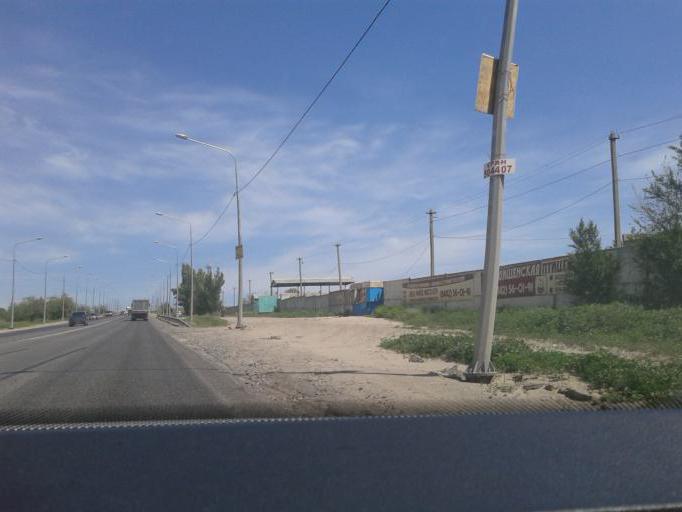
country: RU
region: Volgograd
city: Gorodishche
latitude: 48.8025
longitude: 44.5223
